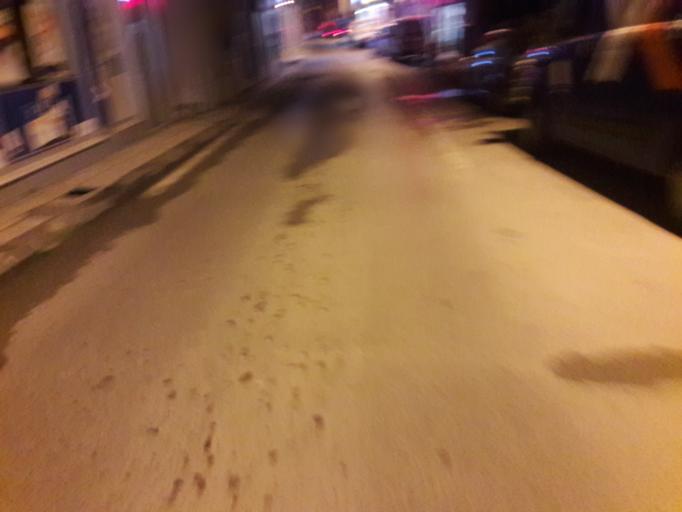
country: TR
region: Sinop
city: Sinop
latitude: 42.0250
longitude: 35.1472
